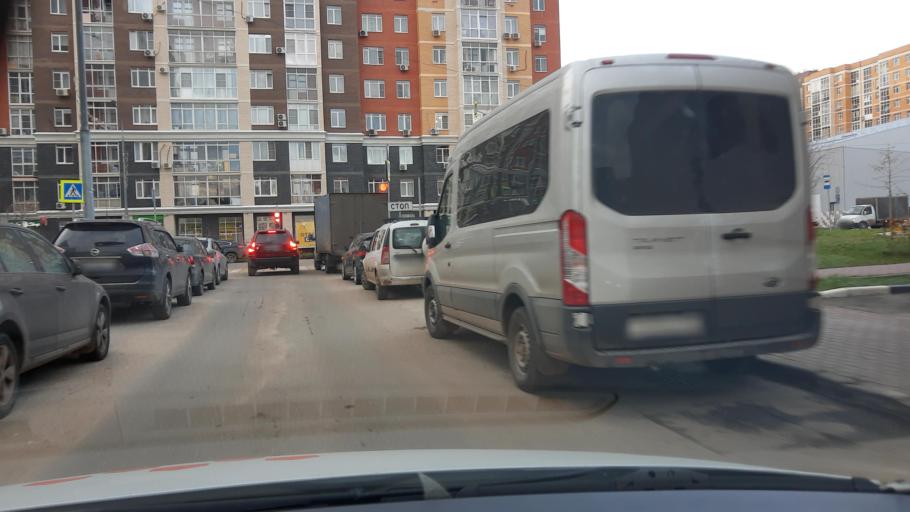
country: RU
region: Moskovskaya
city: Kommunarka
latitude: 55.5699
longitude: 37.4927
